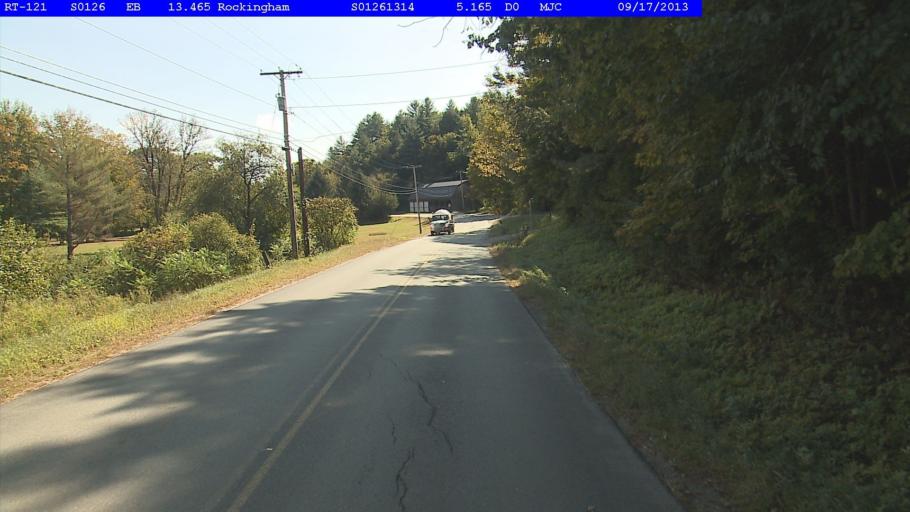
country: US
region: Vermont
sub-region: Windham County
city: Bellows Falls
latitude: 43.1262
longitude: -72.4774
